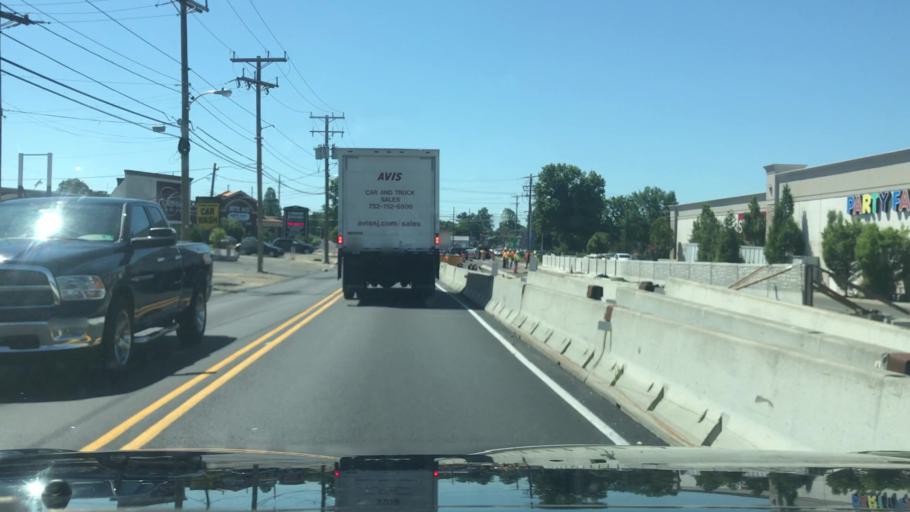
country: US
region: New Jersey
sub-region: Ocean County
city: Toms River
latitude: 39.9655
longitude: -74.2017
